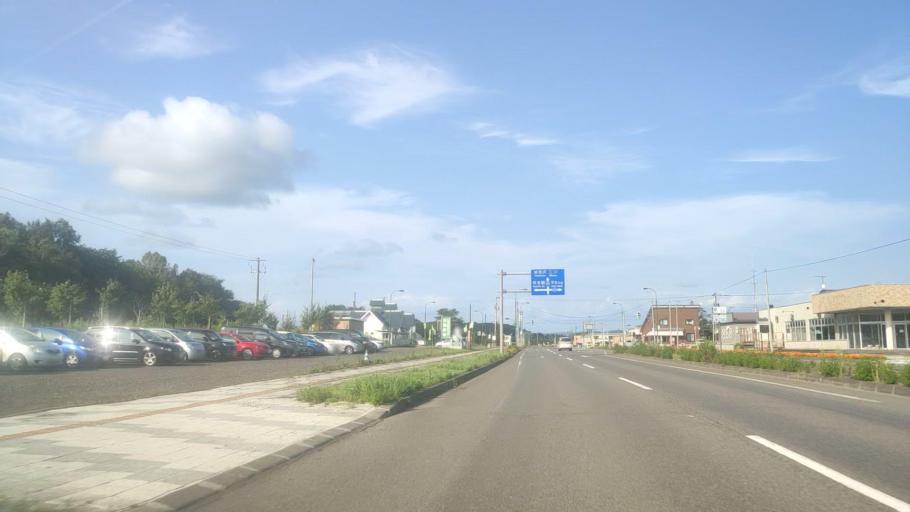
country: JP
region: Hokkaido
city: Chitose
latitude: 42.7643
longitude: 141.8135
